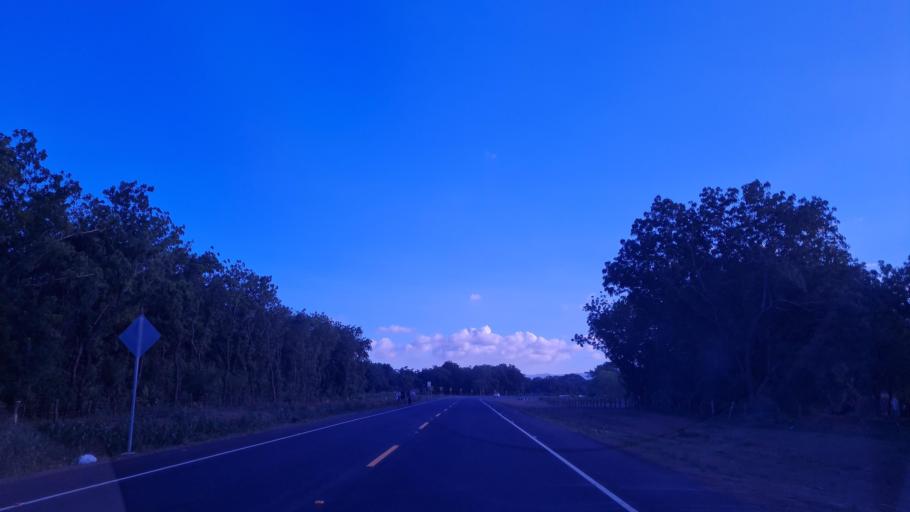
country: NI
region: Masaya
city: Ticuantepe
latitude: 12.0943
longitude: -86.1611
